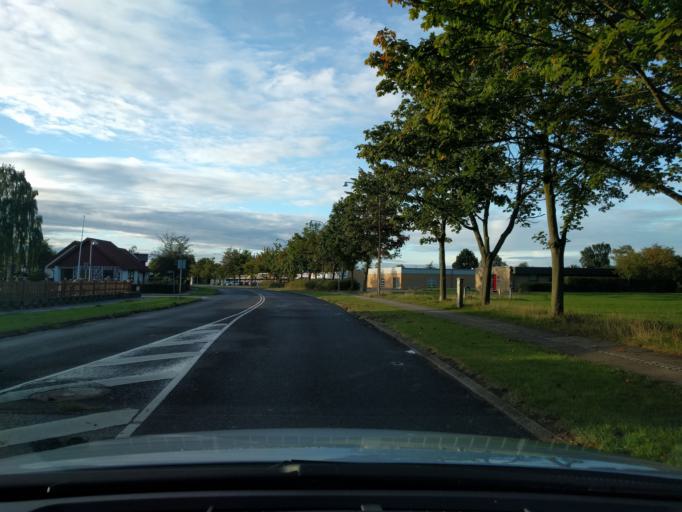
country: DK
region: South Denmark
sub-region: Odense Kommune
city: Bullerup
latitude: 55.4263
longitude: 10.4774
